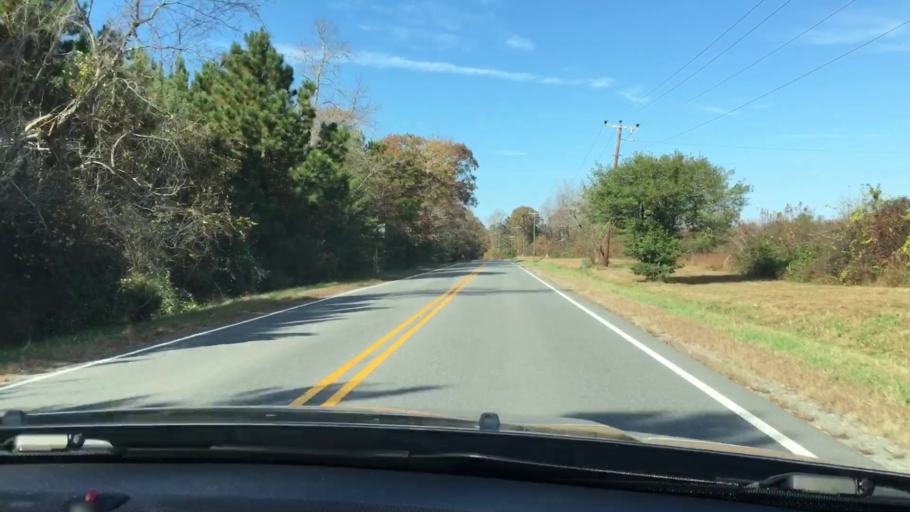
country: US
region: Virginia
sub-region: King and Queen County
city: King and Queen Court House
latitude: 37.6083
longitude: -76.9104
